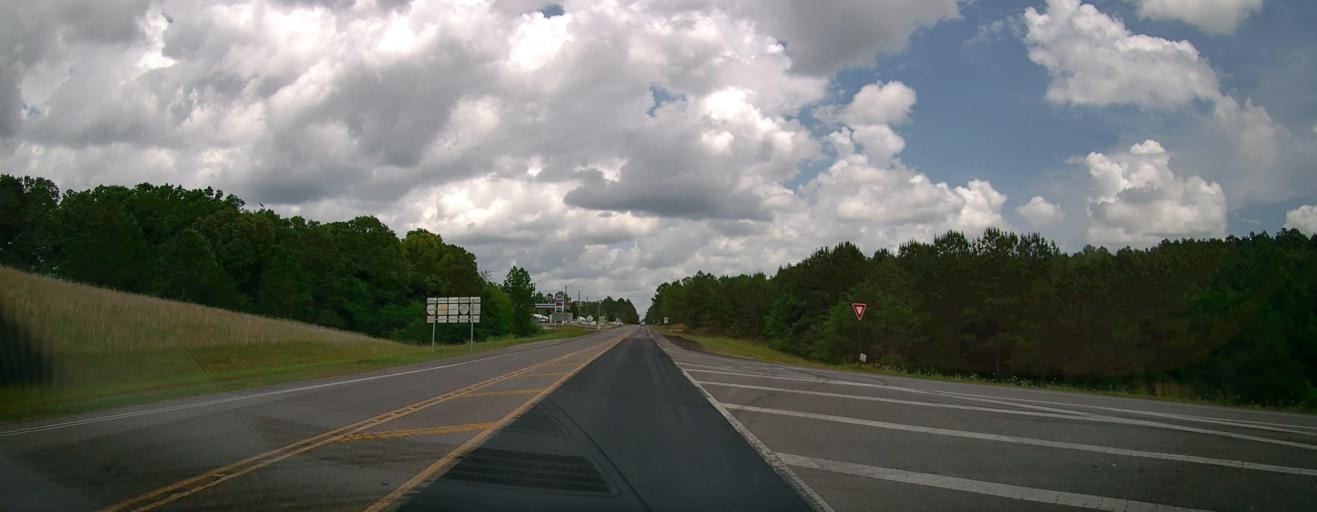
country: US
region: Alabama
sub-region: Marion County
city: Hamilton
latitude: 34.1208
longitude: -88.0440
